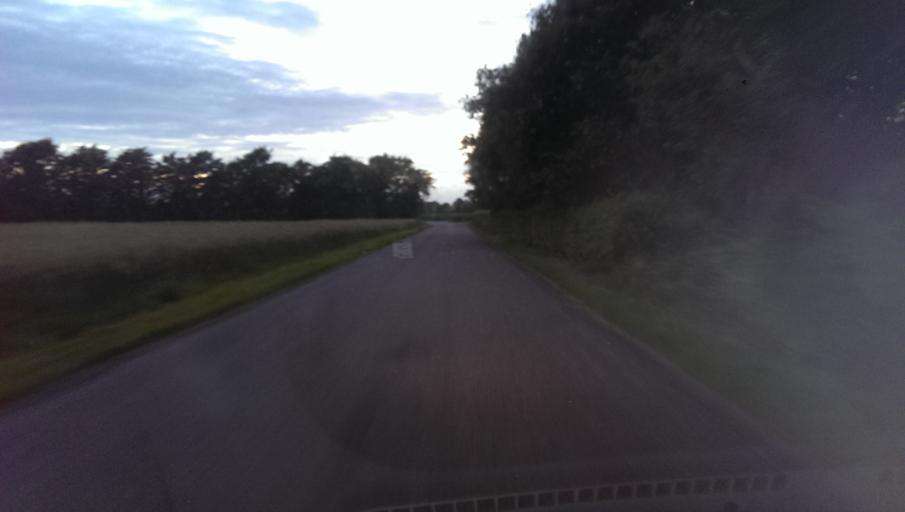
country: DK
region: South Denmark
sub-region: Esbjerg Kommune
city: Esbjerg
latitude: 55.5290
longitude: 8.4896
